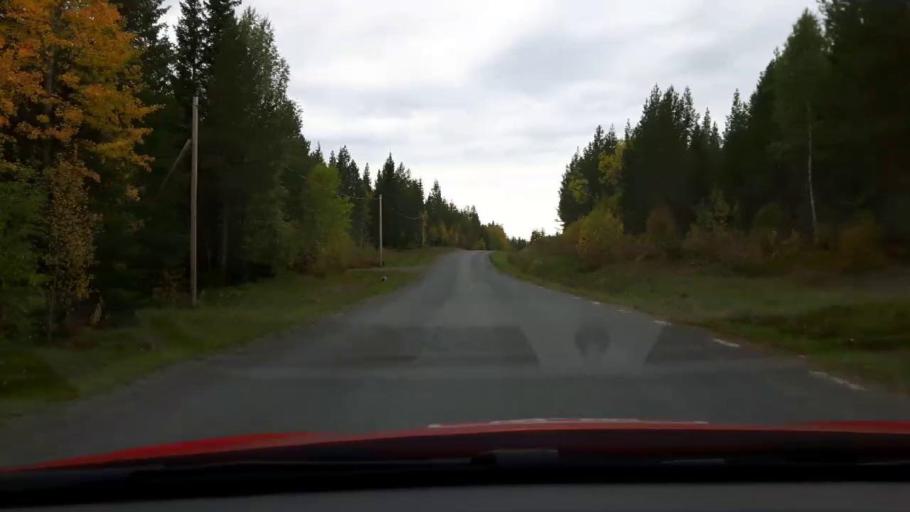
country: SE
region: Jaemtland
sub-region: Krokoms Kommun
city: Krokom
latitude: 63.2207
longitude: 14.1286
